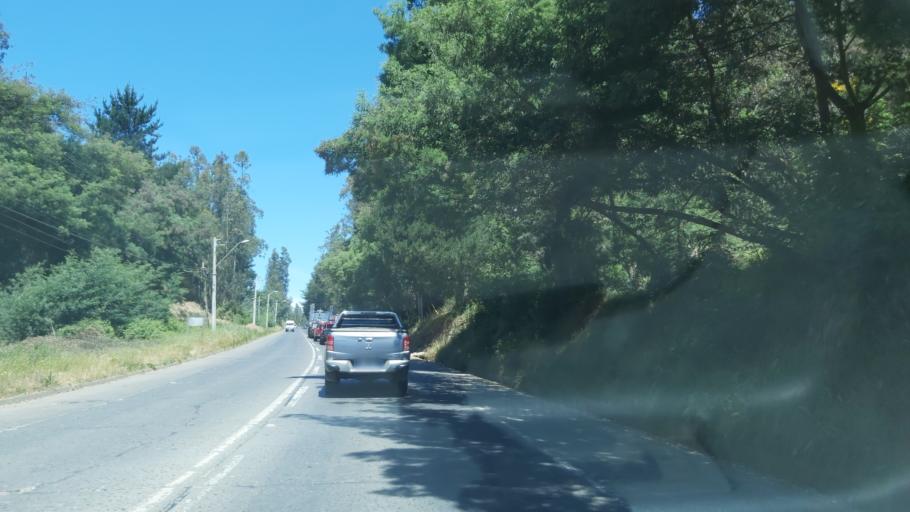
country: CL
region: Maule
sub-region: Provincia de Talca
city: Constitucion
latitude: -35.3546
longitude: -72.4101
